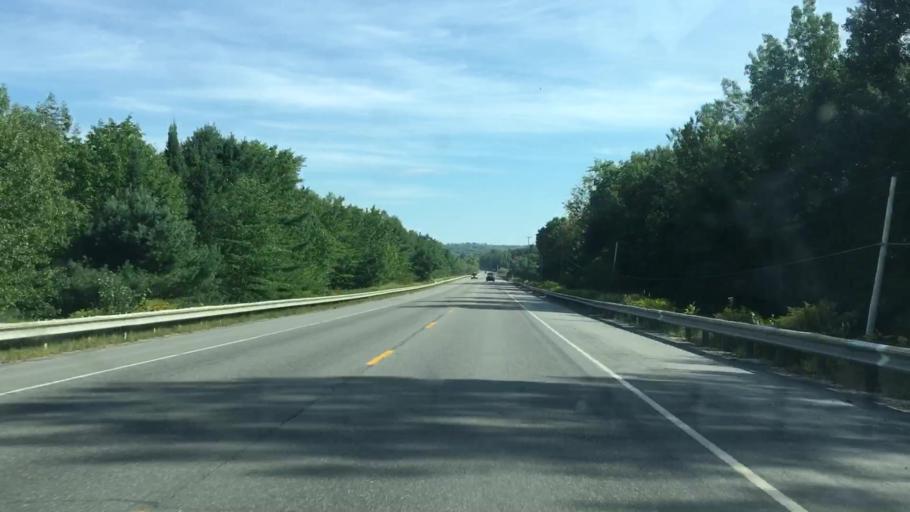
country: US
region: Maine
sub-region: Penobscot County
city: Lincoln
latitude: 45.3663
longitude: -68.5519
